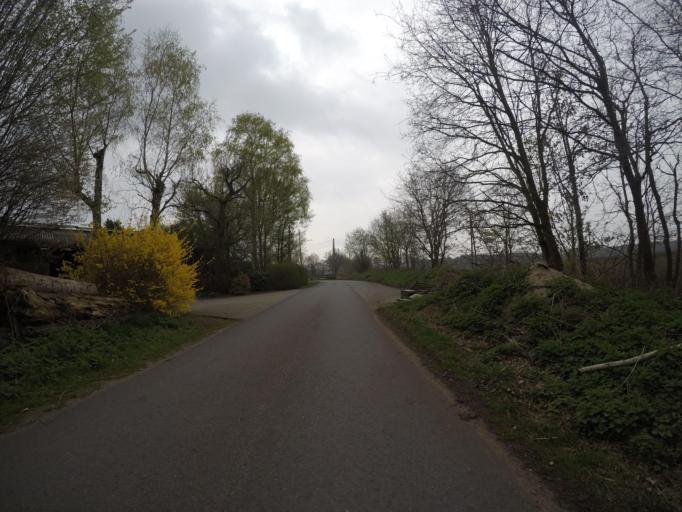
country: NL
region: Gelderland
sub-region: Gemeente Aalten
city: Bredevoort
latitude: 51.9038
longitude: 6.6524
